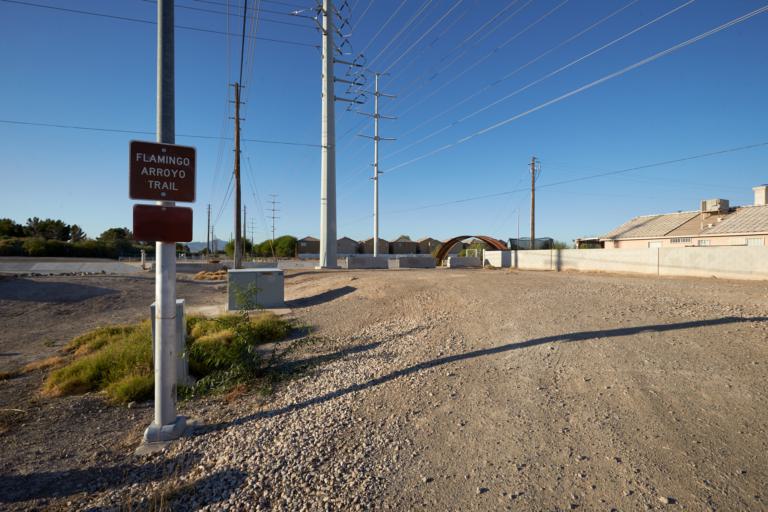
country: US
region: Nevada
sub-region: Clark County
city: Winchester
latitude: 36.1405
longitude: -115.0475
